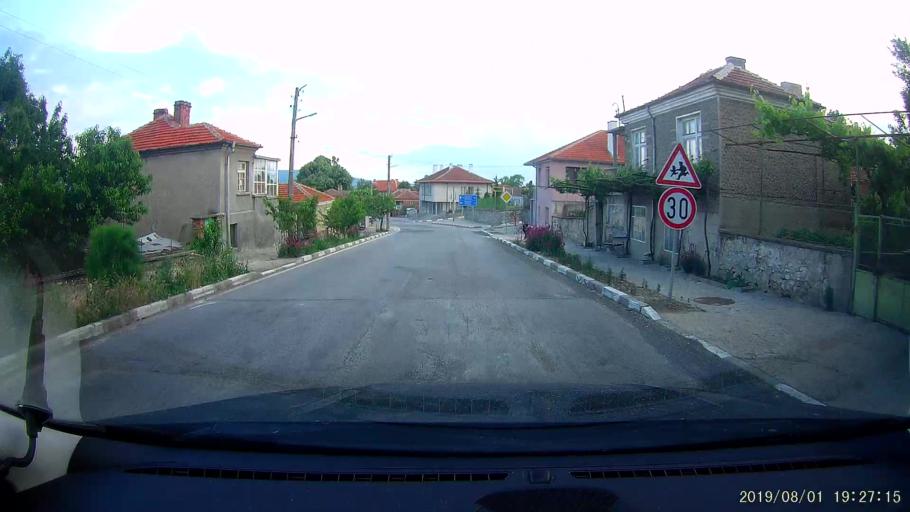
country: BG
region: Burgas
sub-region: Obshtina Sungurlare
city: Sungurlare
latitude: 42.8514
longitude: 26.9312
